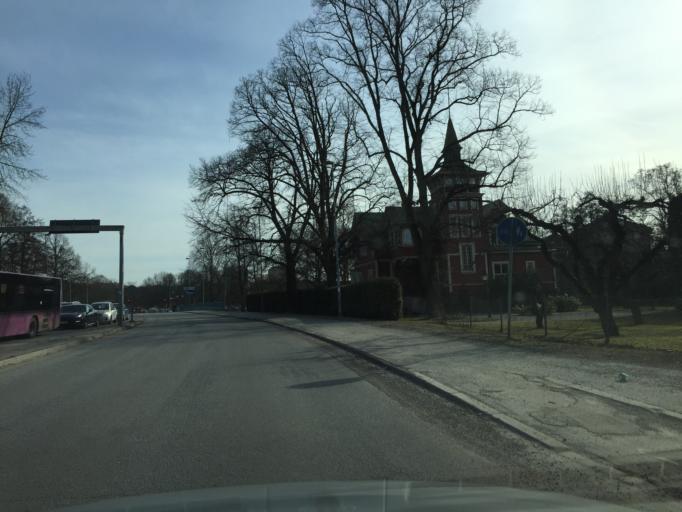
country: SE
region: OErebro
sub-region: Orebro Kommun
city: Orebro
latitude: 59.2724
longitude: 15.2009
